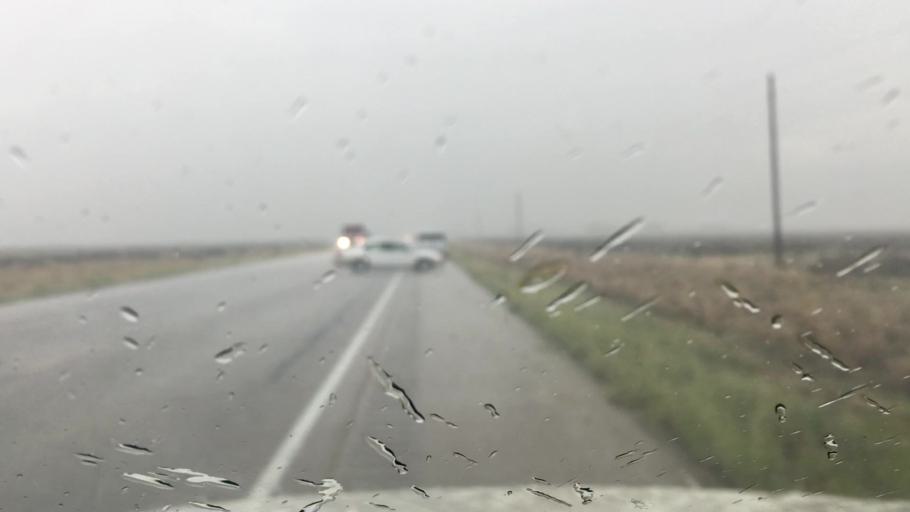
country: US
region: New Mexico
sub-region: Lea County
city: Lovington
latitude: 33.2570
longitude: -103.2169
